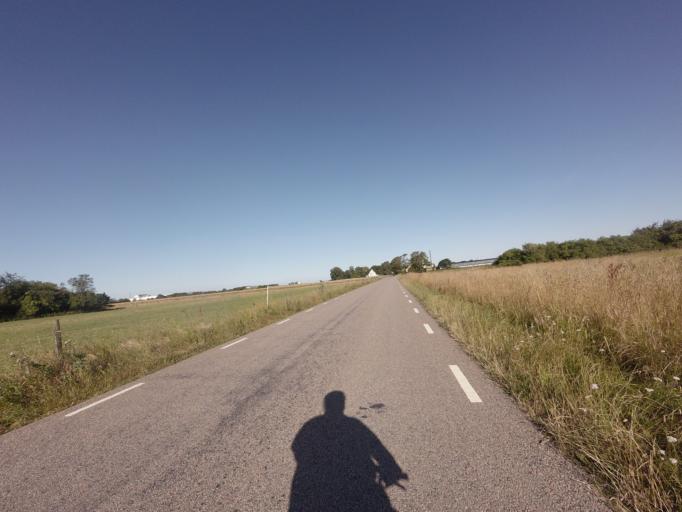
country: SE
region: Skane
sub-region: Hoganas Kommun
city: Hoganas
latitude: 56.1646
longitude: 12.5981
